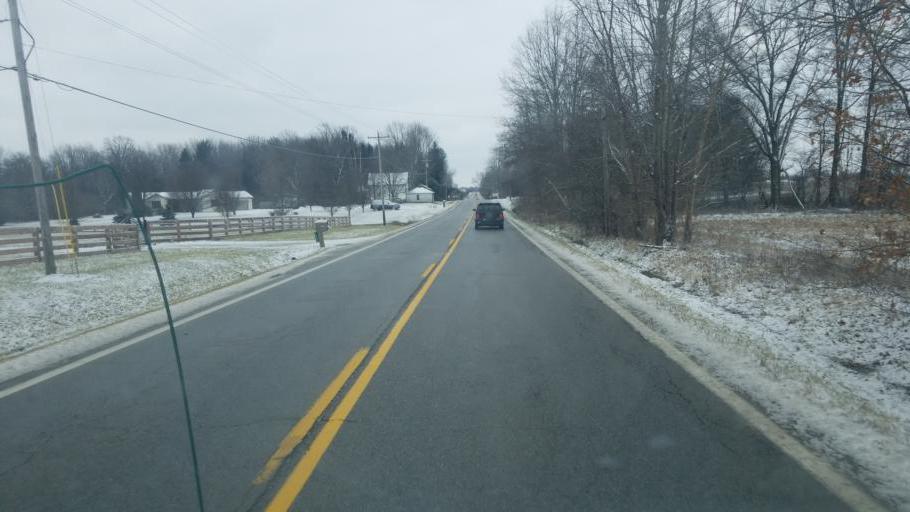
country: US
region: Ohio
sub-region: Licking County
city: Johnstown
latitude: 40.1994
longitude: -82.7701
